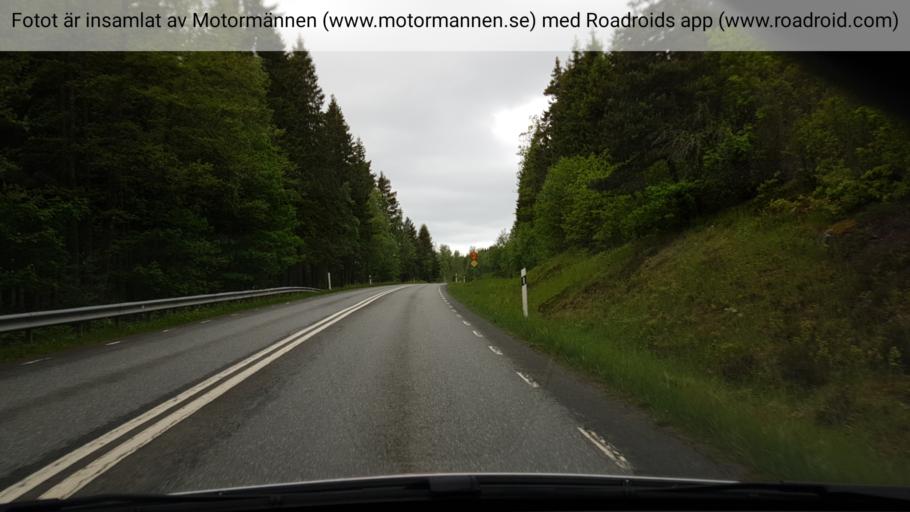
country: SE
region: Joenkoeping
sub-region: Jonkopings Kommun
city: Asa
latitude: 58.0088
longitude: 14.5471
